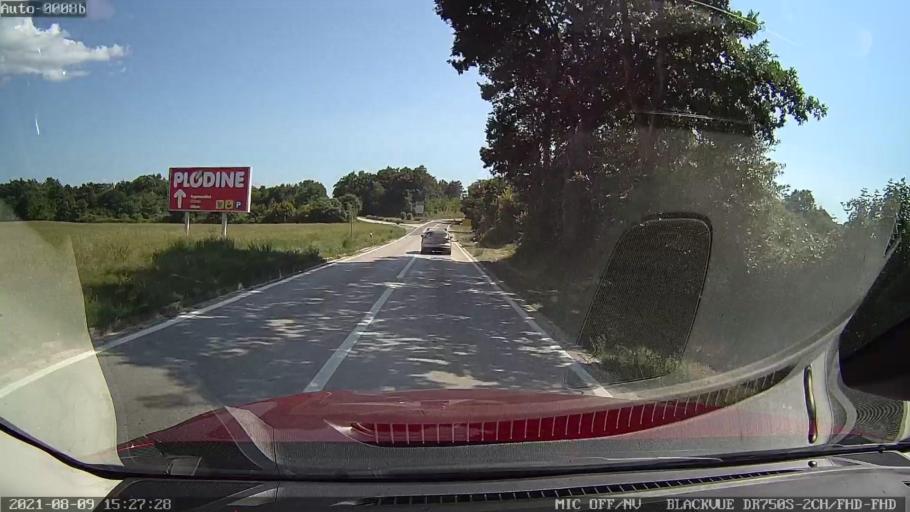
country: HR
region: Istarska
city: Pazin
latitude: 45.1528
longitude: 13.9067
